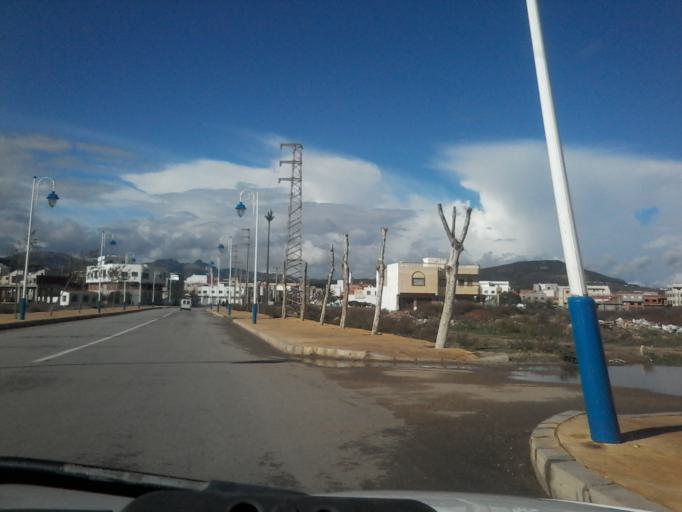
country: MA
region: Tanger-Tetouan
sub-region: Tetouan
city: Martil
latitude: 35.6947
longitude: -5.3430
